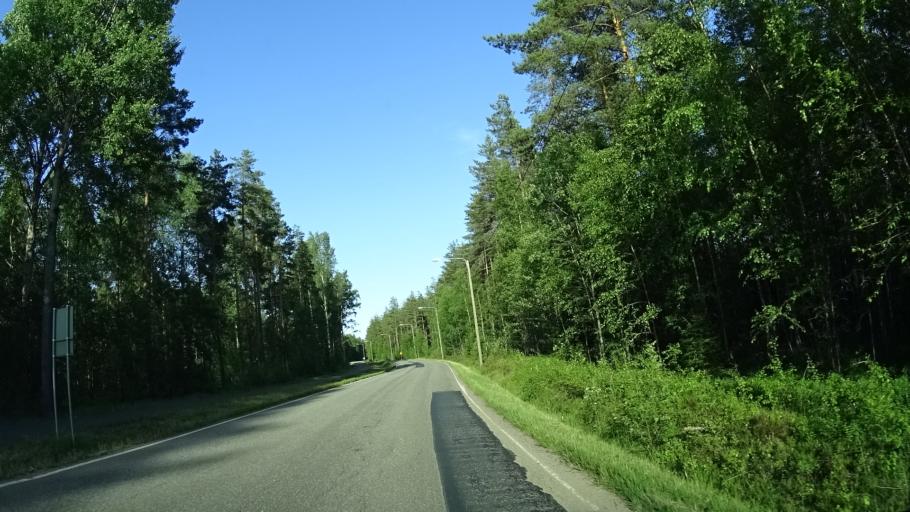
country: FI
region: Satakunta
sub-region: Pori
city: Harjavalta
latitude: 61.2942
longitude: 22.1923
